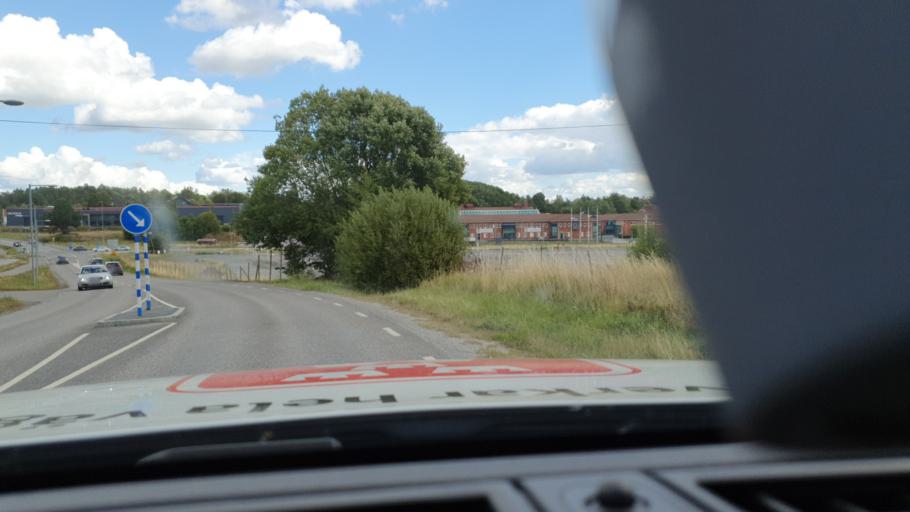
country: SE
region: Stockholm
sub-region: Osterakers Kommun
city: Akersberga
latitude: 59.4821
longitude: 18.2698
